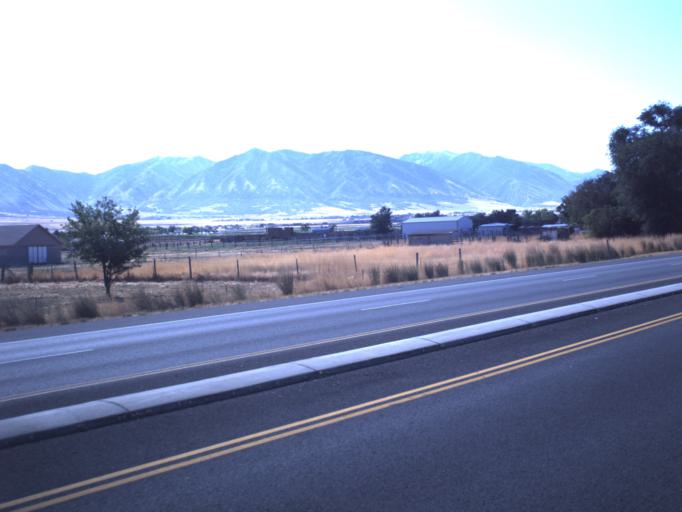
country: US
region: Utah
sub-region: Tooele County
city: Erda
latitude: 40.6187
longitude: -112.2944
